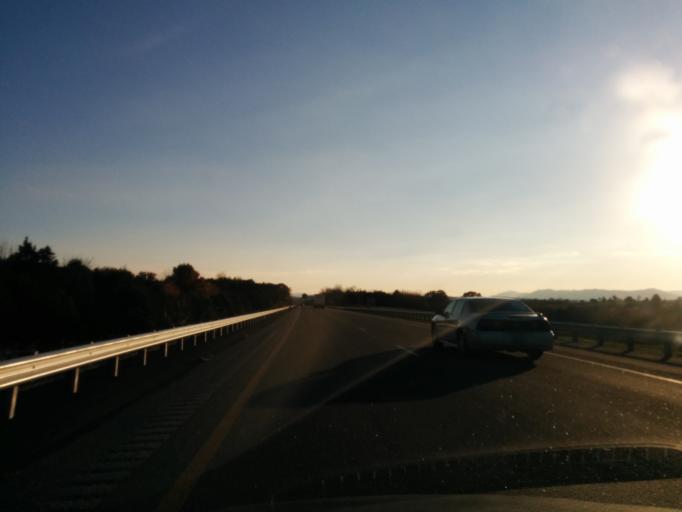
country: US
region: Virginia
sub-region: Rockbridge County
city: East Lexington
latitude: 37.8125
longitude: -79.3858
